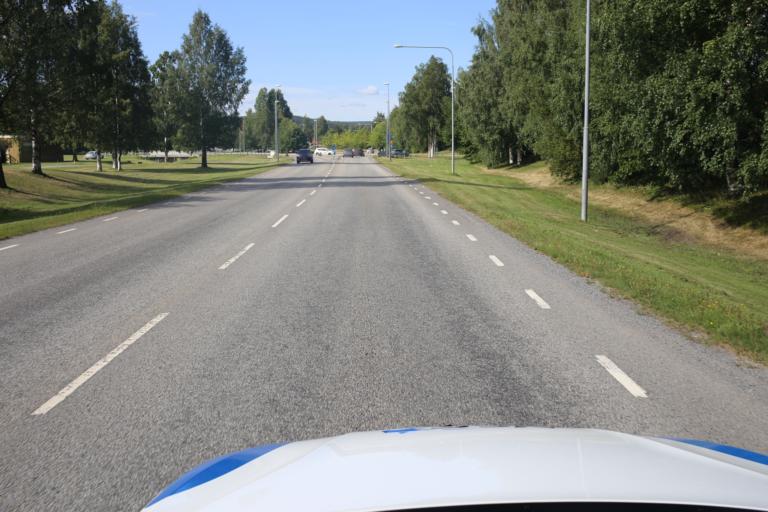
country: SE
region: Vaesterbotten
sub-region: Skelleftea Kommun
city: Skelleftea
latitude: 64.7444
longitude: 20.9671
